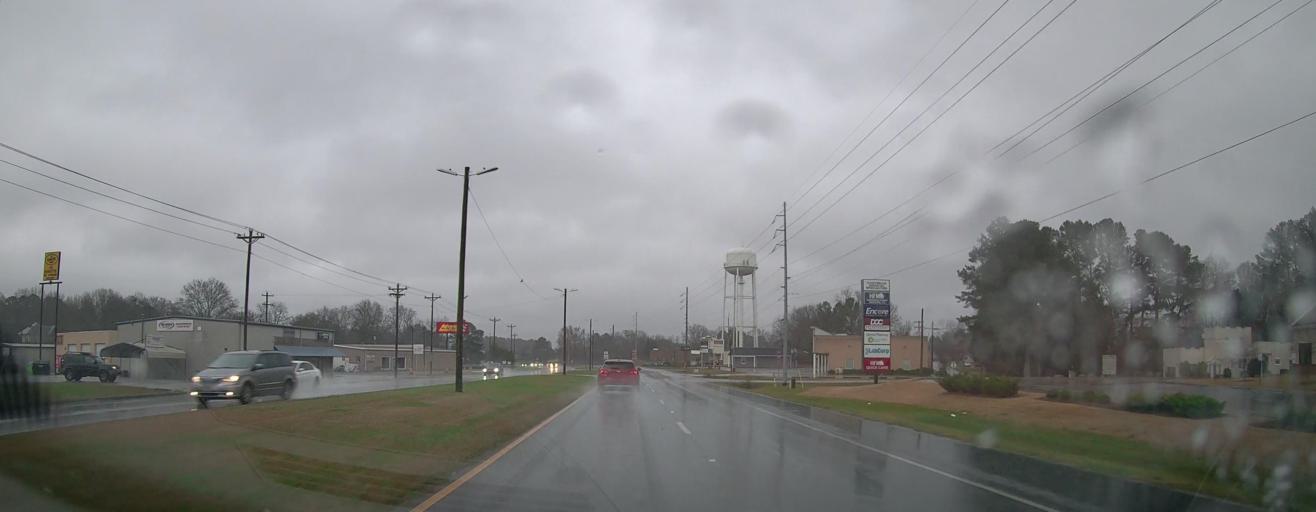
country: US
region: Alabama
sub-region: Morgan County
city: Hartselle
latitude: 34.4379
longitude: -86.9404
